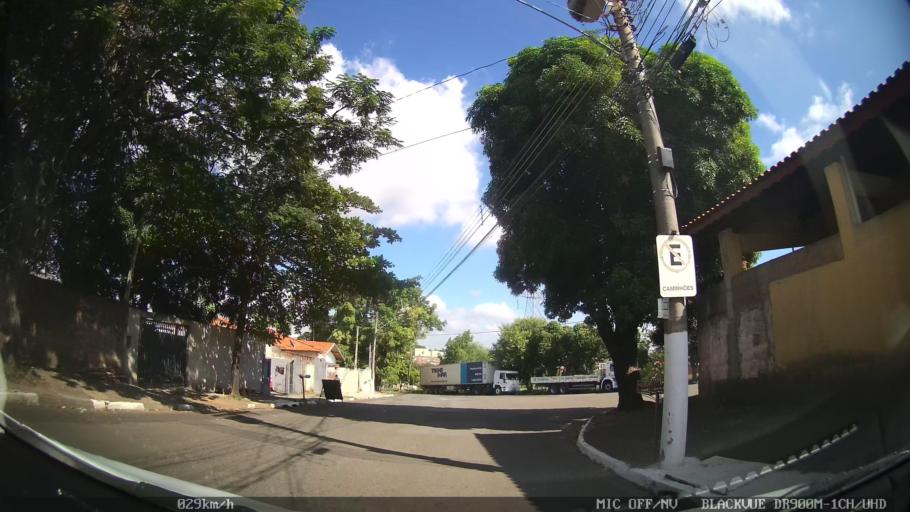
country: BR
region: Sao Paulo
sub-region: Hortolandia
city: Hortolandia
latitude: -22.8925
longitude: -47.1936
